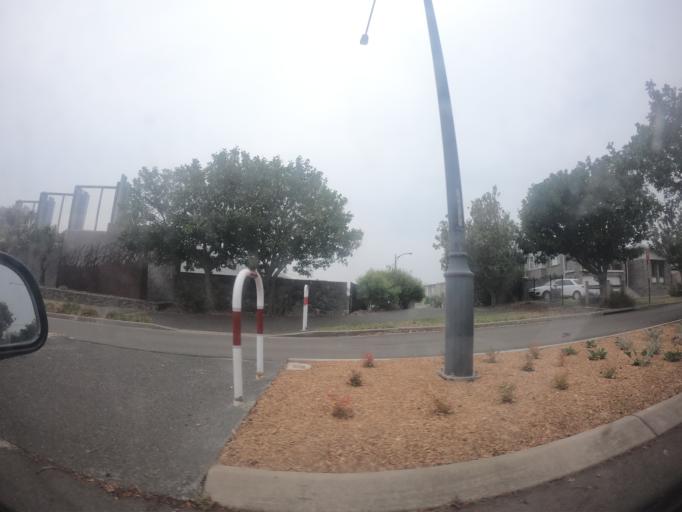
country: AU
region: New South Wales
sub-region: Shellharbour
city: Croom
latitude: -34.5975
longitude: 150.8543
